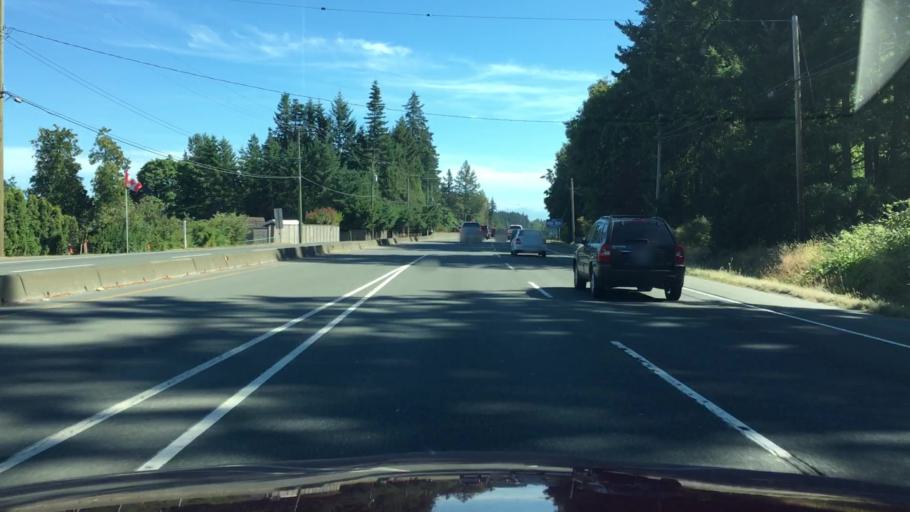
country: CA
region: British Columbia
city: Victoria
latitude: 48.5432
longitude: -123.3904
